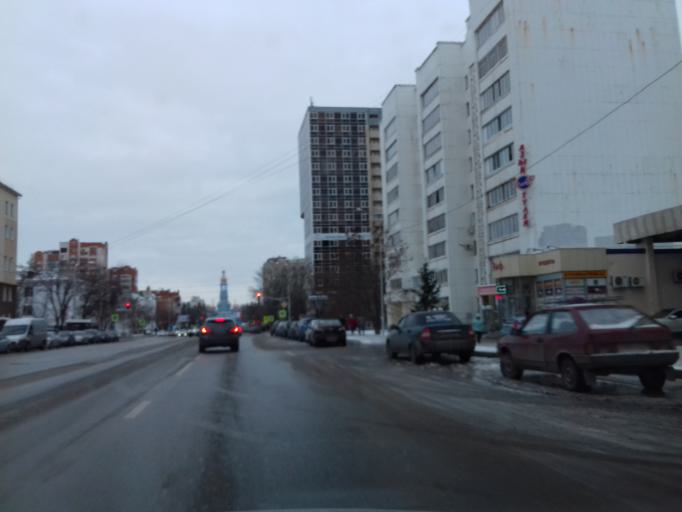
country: RU
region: Bashkortostan
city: Ufa
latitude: 54.7284
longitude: 55.9661
